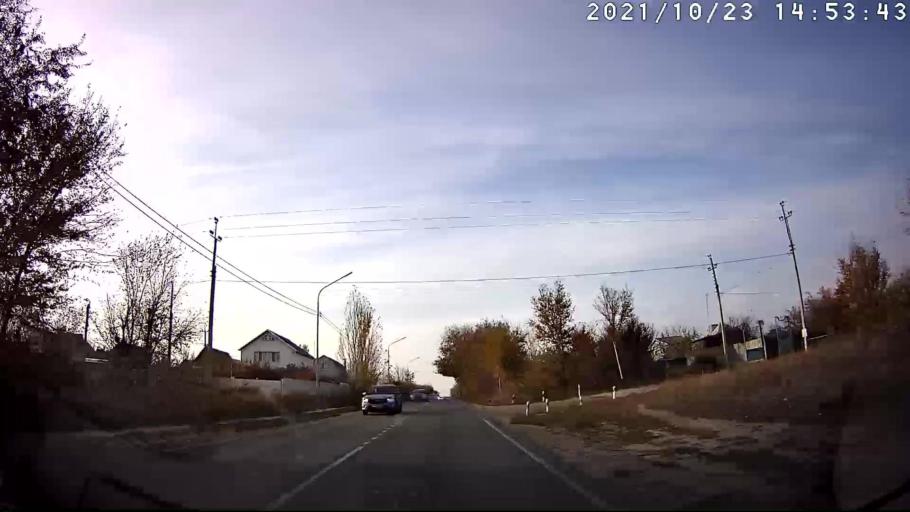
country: RU
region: Volgograd
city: Volgograd
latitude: 48.4428
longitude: 44.4267
